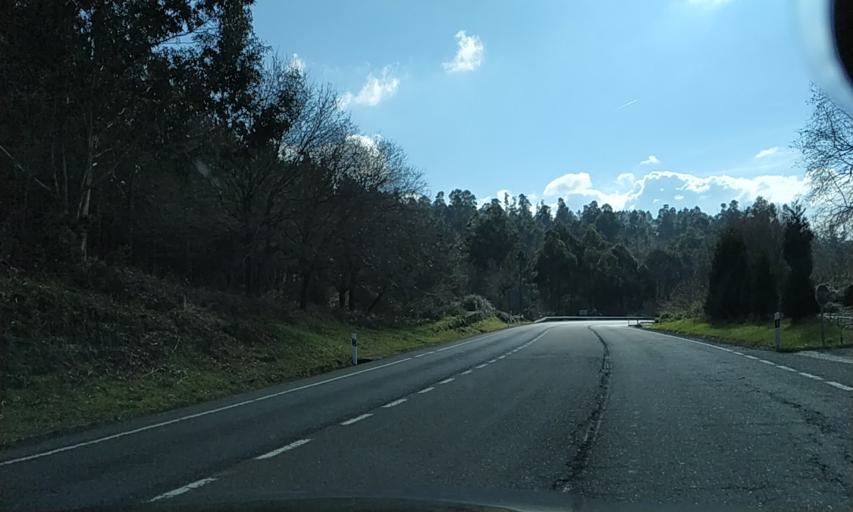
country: ES
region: Galicia
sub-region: Provincia da Coruna
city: Ribeira
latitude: 42.7107
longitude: -8.3847
